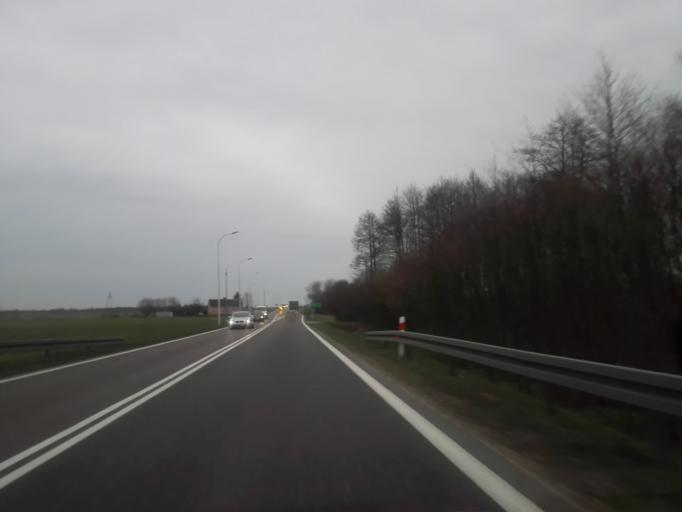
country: PL
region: Podlasie
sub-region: Powiat grajewski
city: Szczuczyn
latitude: 53.4897
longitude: 22.2225
